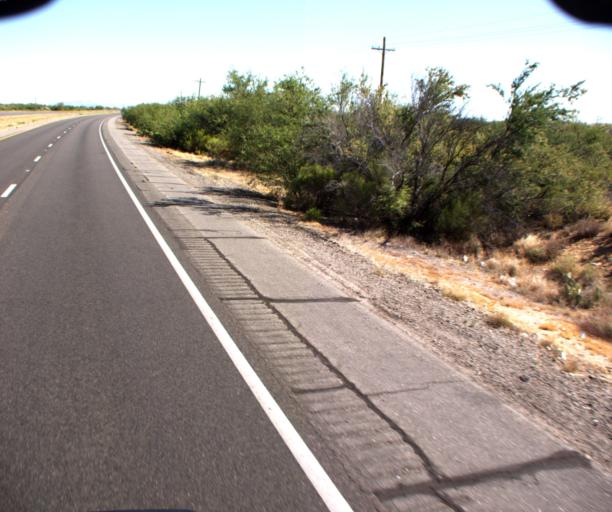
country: US
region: Arizona
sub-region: Pima County
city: Catalina
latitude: 32.5360
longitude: -110.9305
